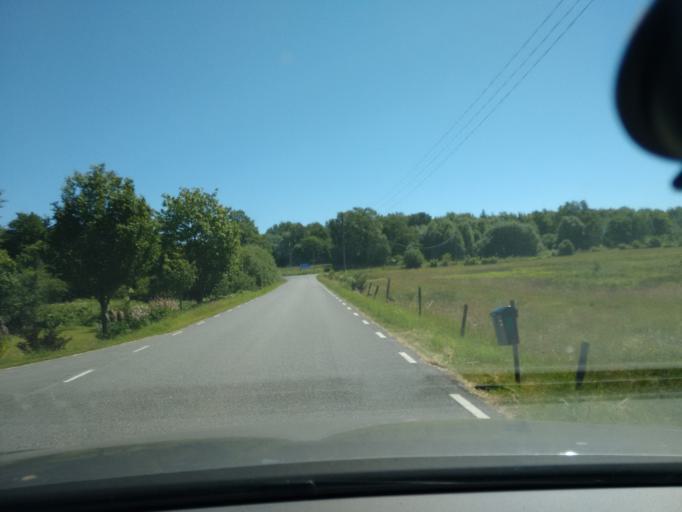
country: SE
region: Skane
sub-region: Kristianstads Kommun
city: Degeberga
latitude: 55.7679
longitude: 14.0000
